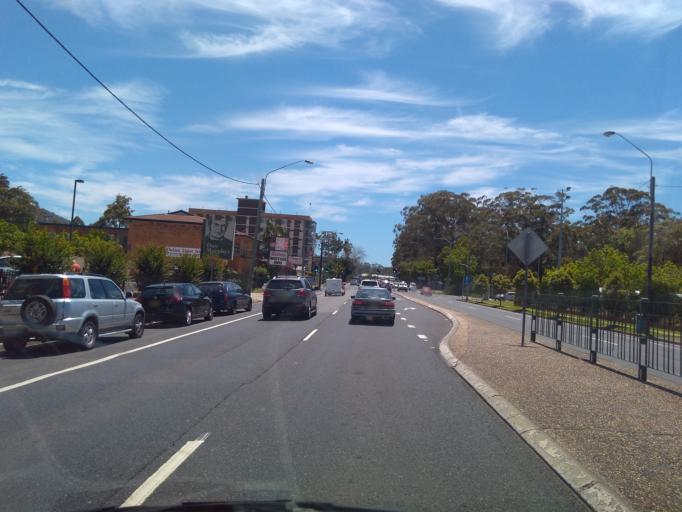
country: AU
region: New South Wales
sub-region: Coffs Harbour
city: Coffs Harbour
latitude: -30.2949
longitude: 153.1152
